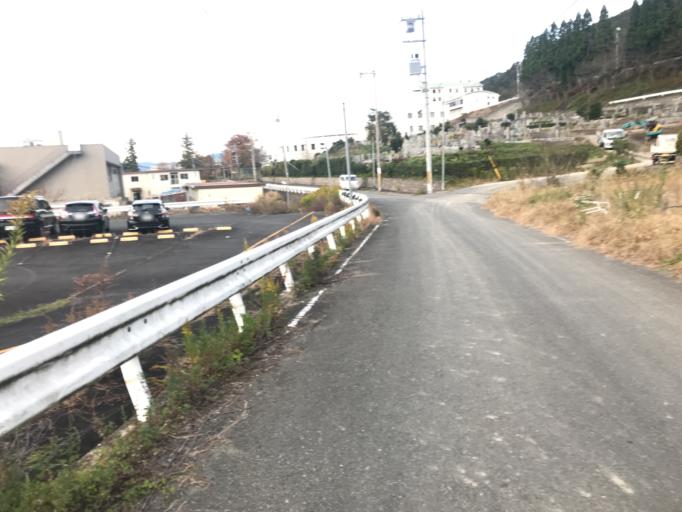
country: JP
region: Kyoto
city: Kameoka
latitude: 34.9922
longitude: 135.5530
